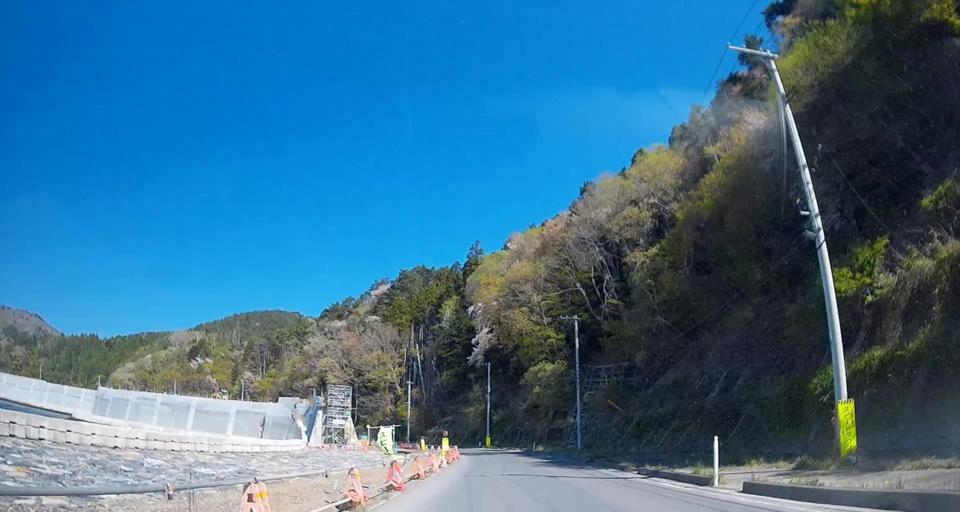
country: JP
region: Miyagi
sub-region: Oshika Gun
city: Onagawa Cho
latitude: 38.5208
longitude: 141.4790
